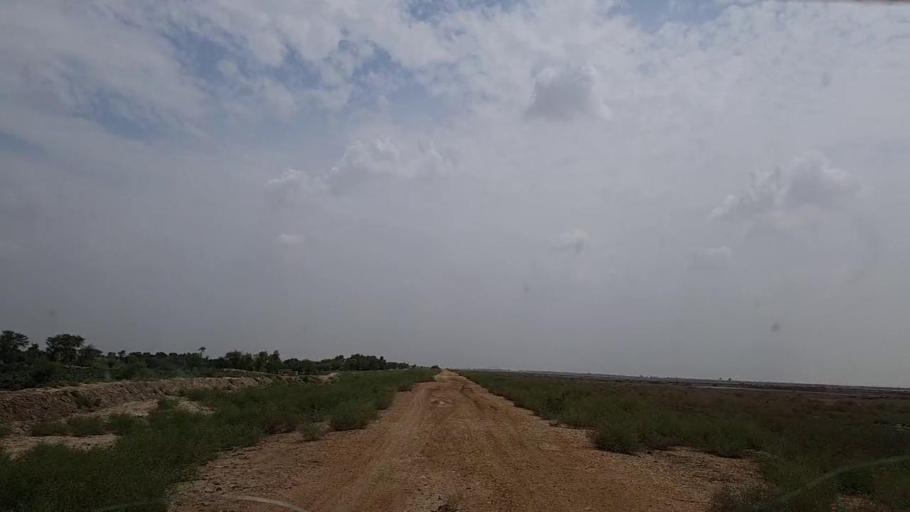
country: PK
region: Sindh
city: Johi
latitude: 26.7927
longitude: 67.6009
